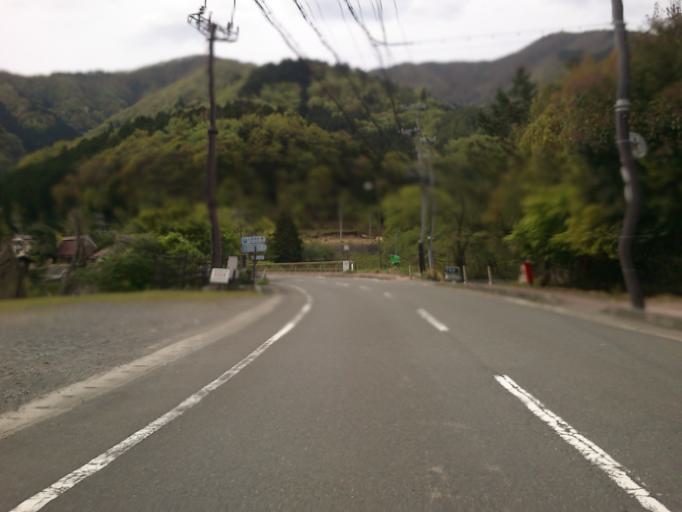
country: JP
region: Kyoto
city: Ayabe
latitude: 35.2692
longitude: 135.4633
